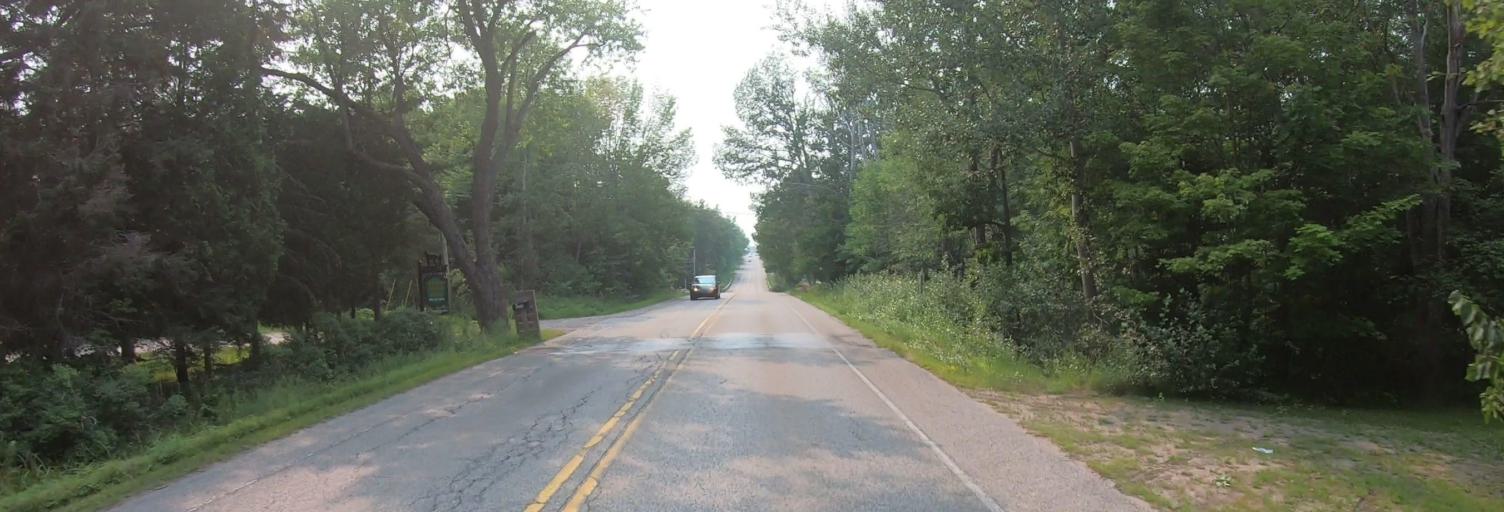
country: US
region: Michigan
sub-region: Chippewa County
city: Sault Ste. Marie
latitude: 46.4630
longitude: -84.3317
